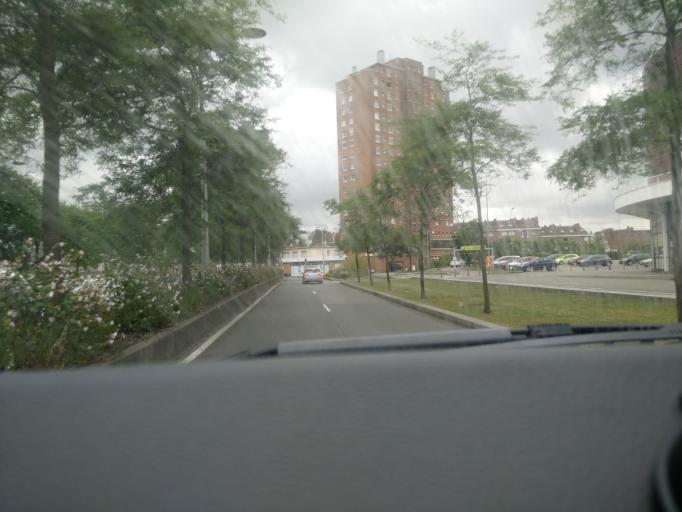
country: FR
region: Nord-Pas-de-Calais
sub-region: Departement du Nord
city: Dunkerque
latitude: 51.0335
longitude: 2.3719
